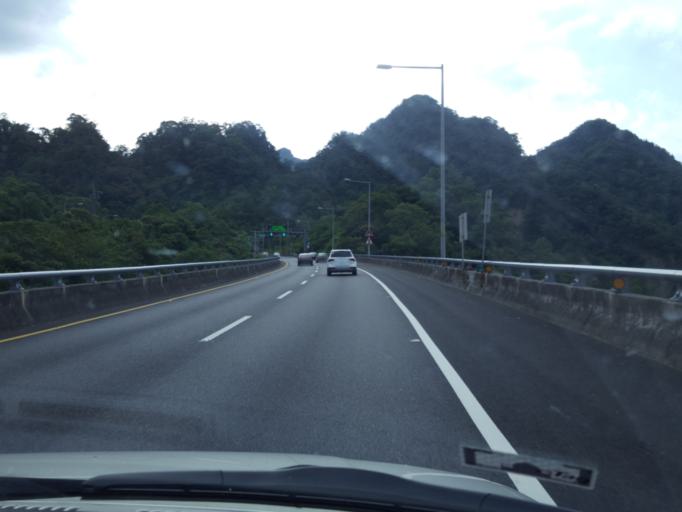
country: TW
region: Taipei
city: Taipei
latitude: 24.9821
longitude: 121.6703
